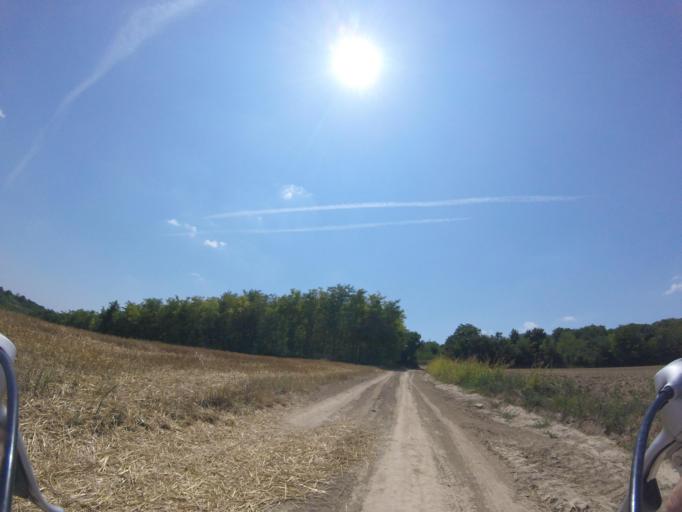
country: HU
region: Somogy
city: Adand
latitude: 46.8053
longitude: 18.1232
